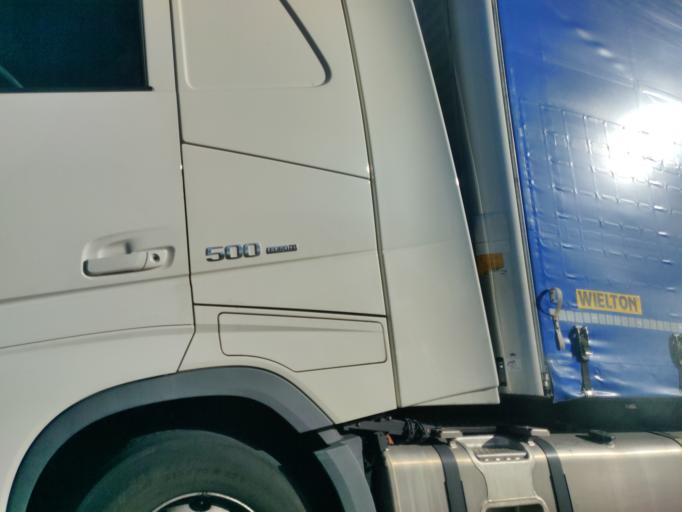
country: IT
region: Tuscany
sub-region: Provincia di Grosseto
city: Gavorrano
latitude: 42.9206
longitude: 10.9762
